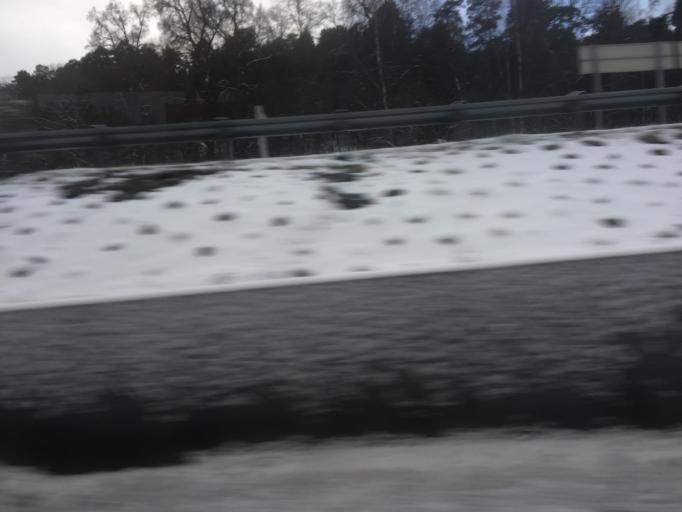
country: NO
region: Akershus
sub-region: Oppegard
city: Kolbotn
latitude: 59.8377
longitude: 10.7791
